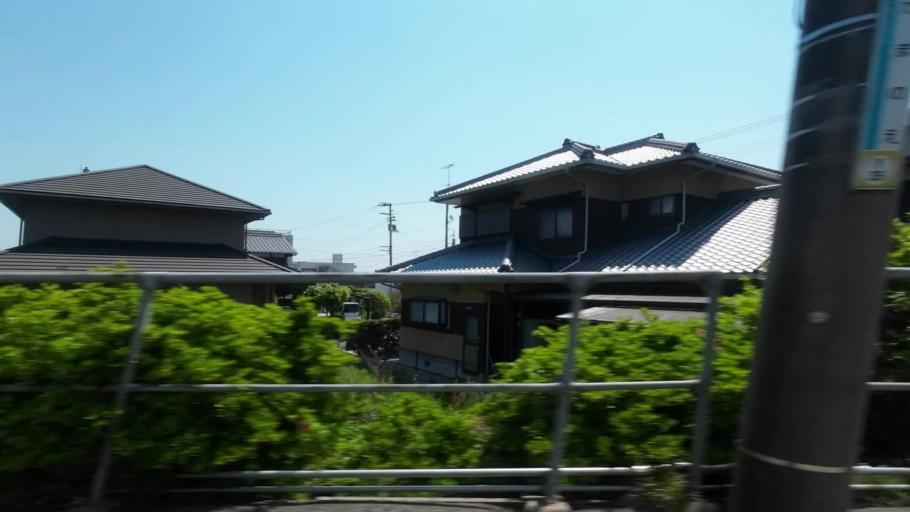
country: JP
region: Ehime
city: Saijo
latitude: 33.9129
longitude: 133.0990
